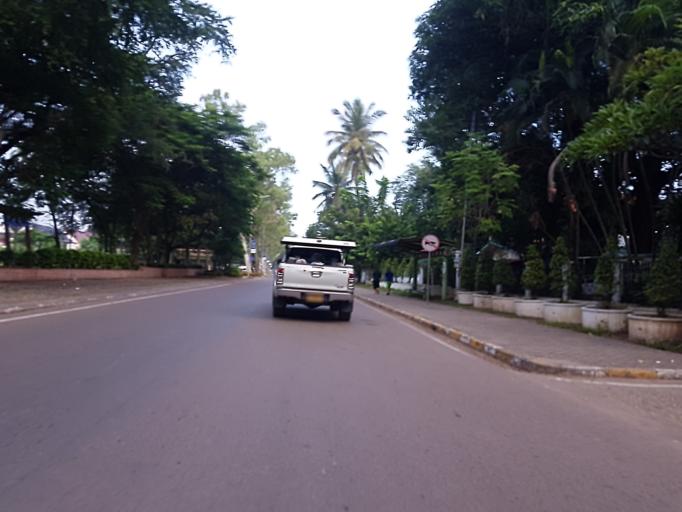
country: LA
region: Vientiane
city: Vientiane
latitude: 17.9587
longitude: 102.6130
